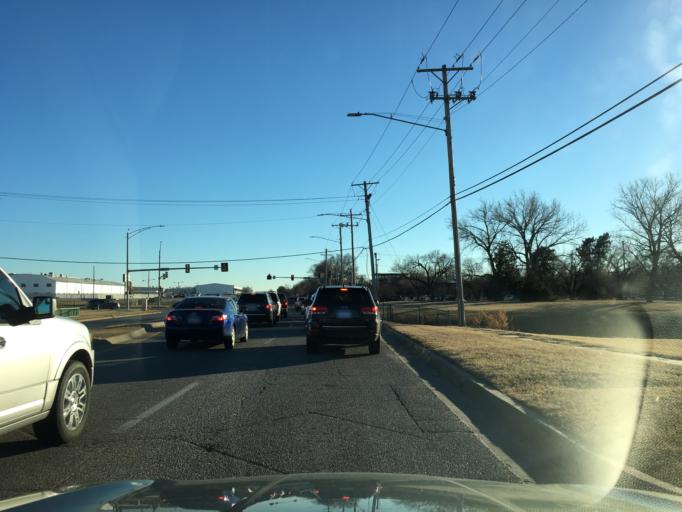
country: US
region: Kansas
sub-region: Sedgwick County
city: Bellaire
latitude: 37.6952
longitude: -97.2263
